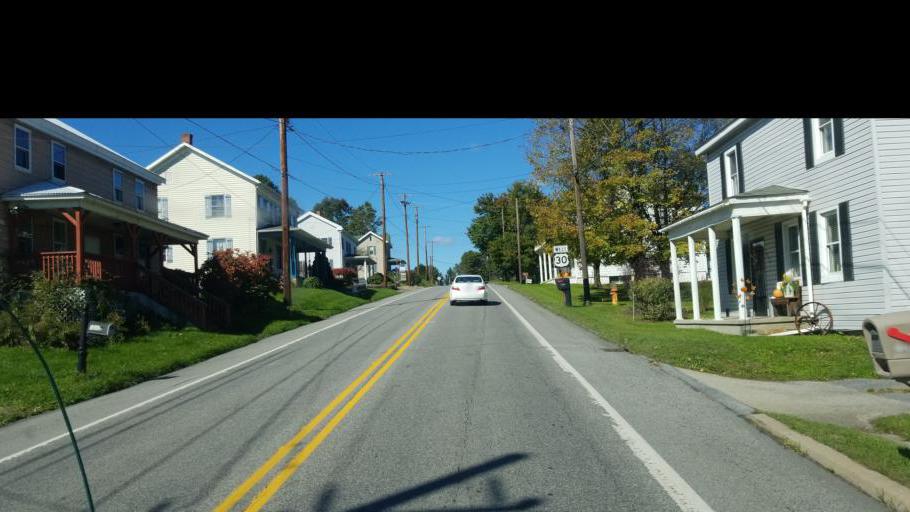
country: US
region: Pennsylvania
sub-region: Somerset County
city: Boswell
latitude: 40.1518
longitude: -79.0501
